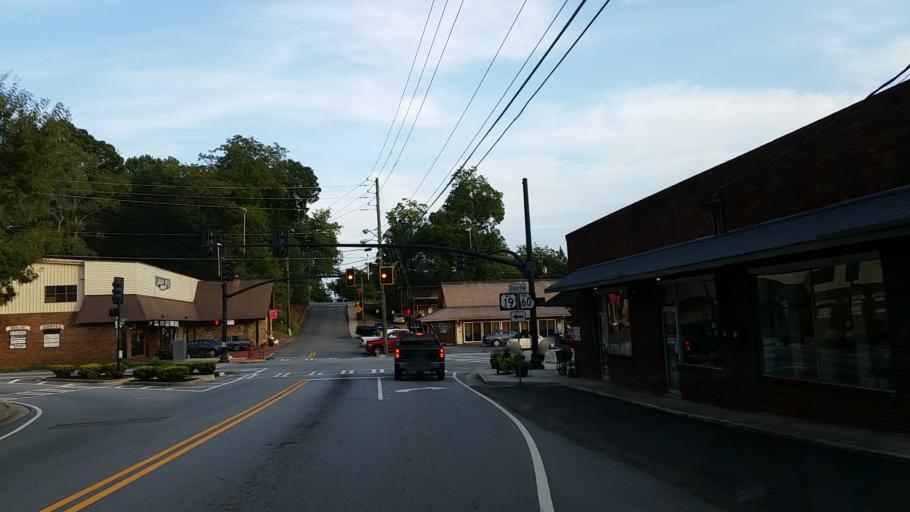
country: US
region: Georgia
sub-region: Lumpkin County
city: Dahlonega
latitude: 34.5340
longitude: -83.9836
